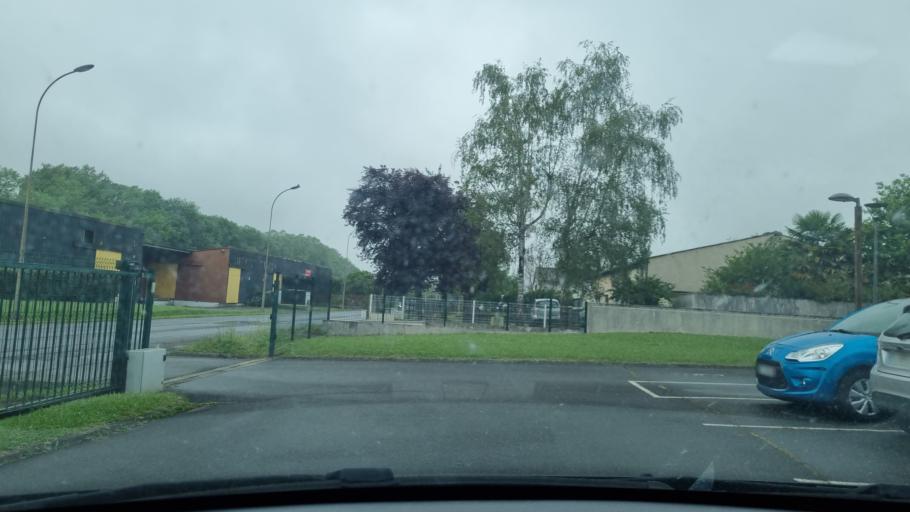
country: FR
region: Aquitaine
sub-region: Departement des Pyrenees-Atlantiques
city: Idron
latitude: 43.3184
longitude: -0.3224
